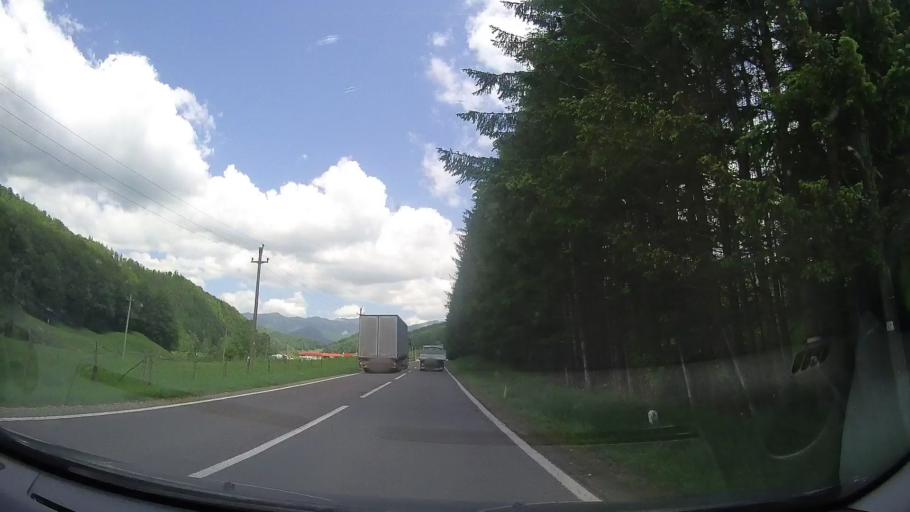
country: RO
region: Prahova
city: Maneciu
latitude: 45.4160
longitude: 25.9429
